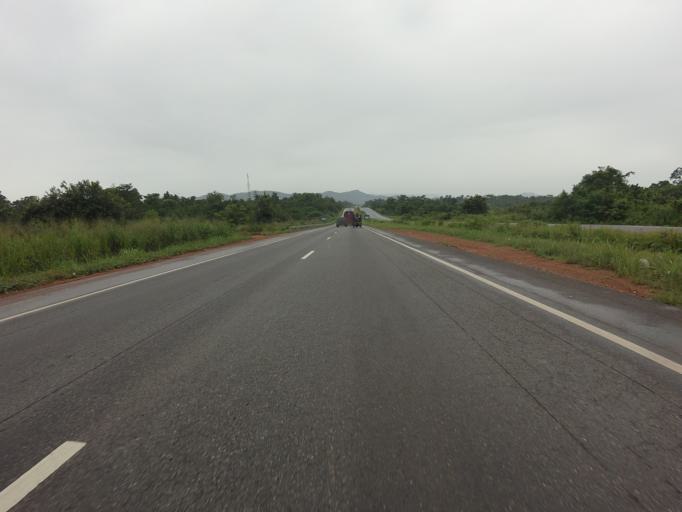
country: GH
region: Eastern
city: Suhum
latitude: 6.0799
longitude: -0.4731
